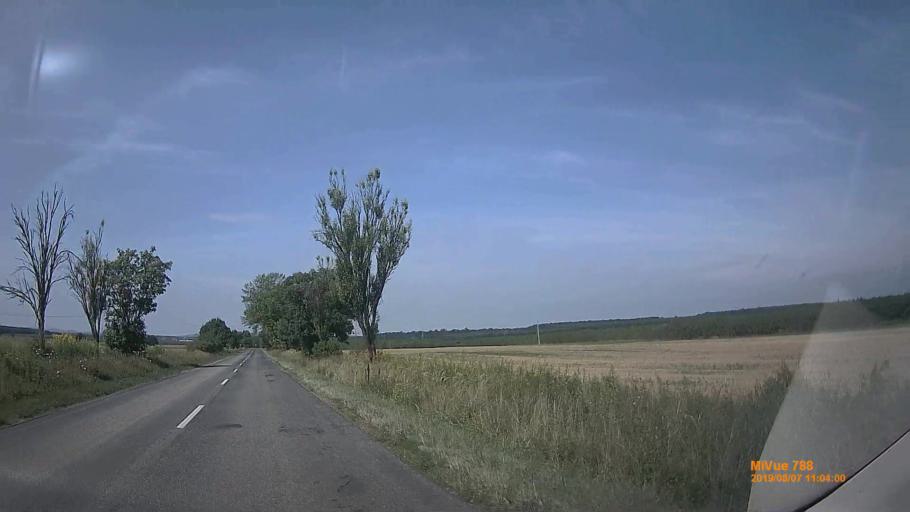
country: HU
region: Veszprem
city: Ajka
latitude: 47.0218
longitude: 17.5016
